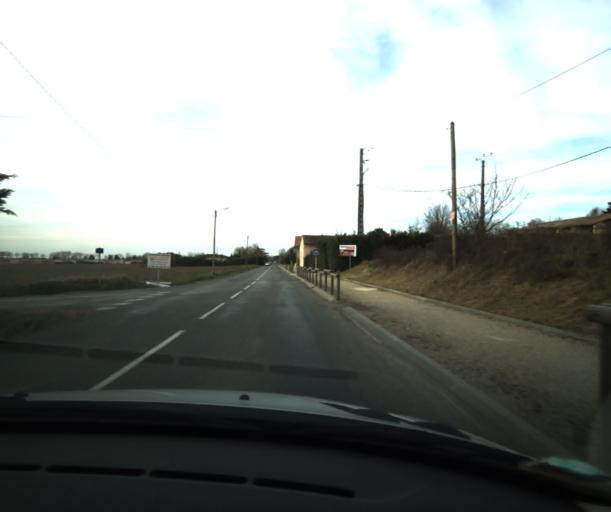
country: FR
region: Midi-Pyrenees
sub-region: Departement du Tarn-et-Garonne
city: Montech
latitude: 43.9493
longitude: 1.2334
